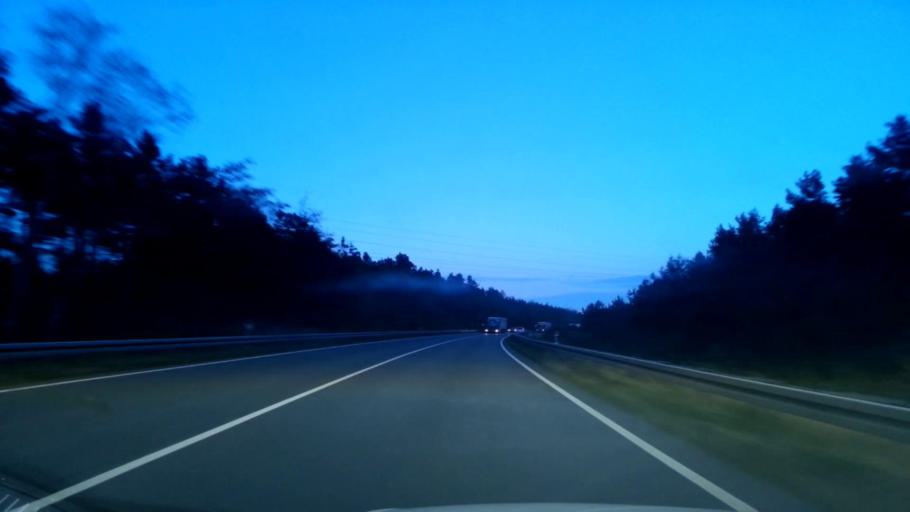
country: DE
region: Bavaria
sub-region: Upper Franconia
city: Strullendorf
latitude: 49.8555
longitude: 10.9552
